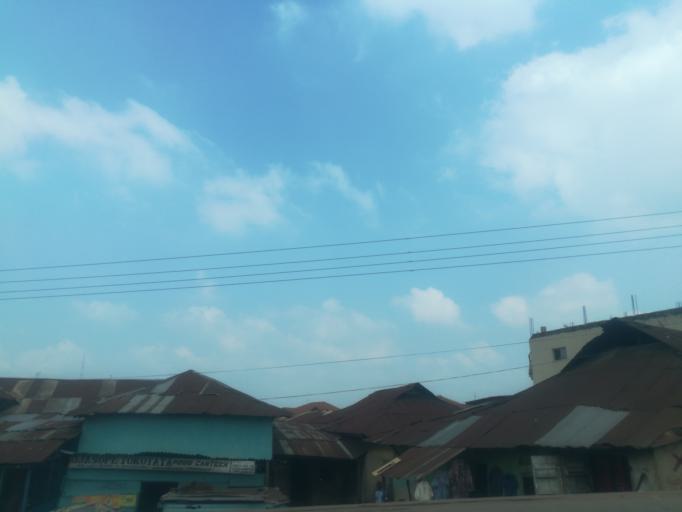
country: NG
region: Oyo
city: Ibadan
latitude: 7.3893
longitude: 3.9086
